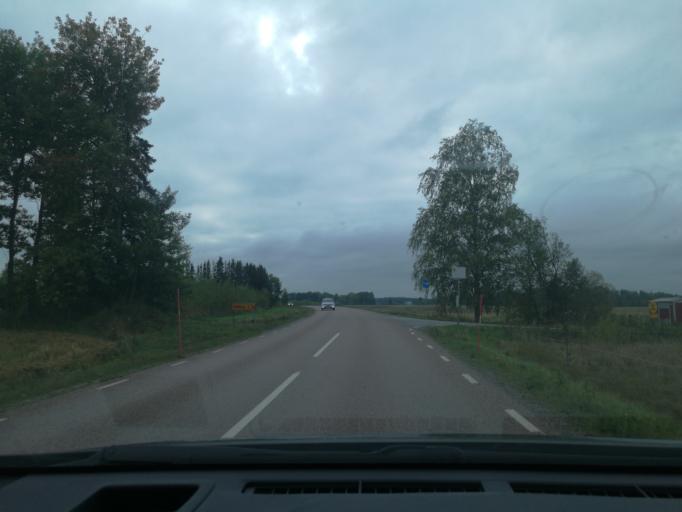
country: SE
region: Vaestmanland
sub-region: Vasteras
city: Tillberga
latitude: 59.6949
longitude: 16.6247
